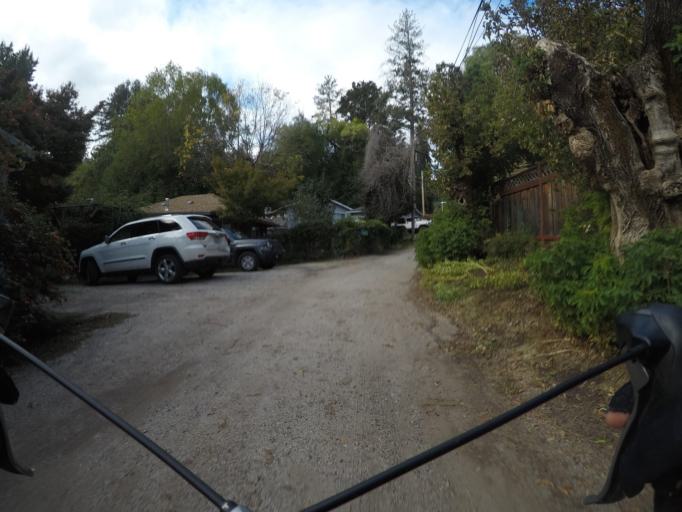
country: US
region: California
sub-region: Santa Cruz County
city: Ben Lomond
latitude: 37.0827
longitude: -122.0820
